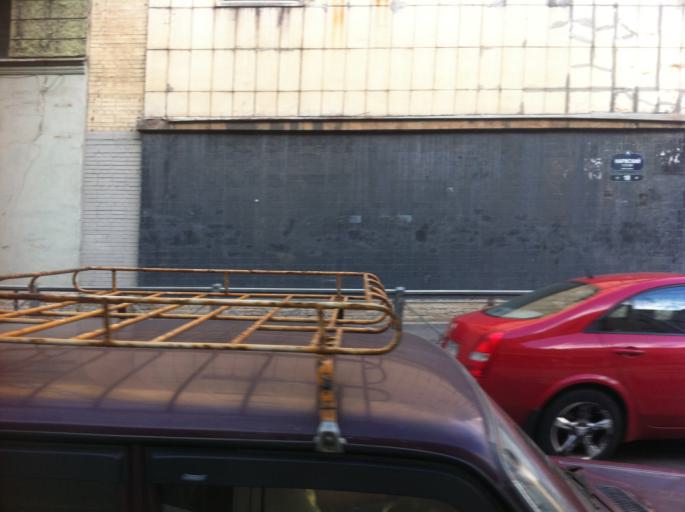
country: RU
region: St.-Petersburg
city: Admiralteisky
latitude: 59.9036
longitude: 30.2741
